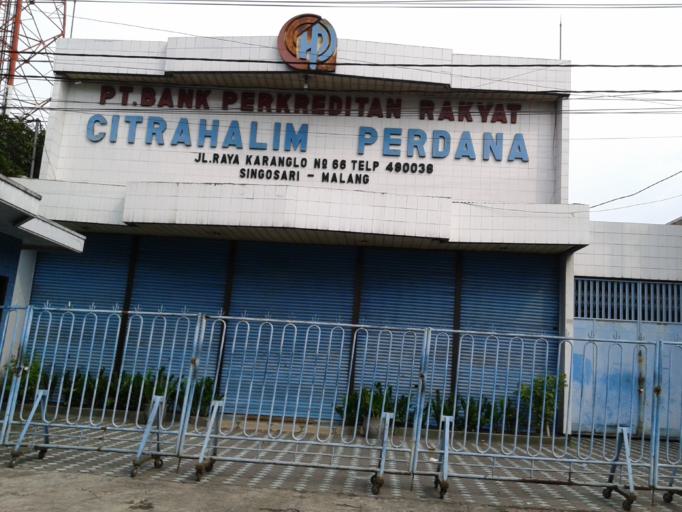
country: ID
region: East Java
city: Singosari
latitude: -7.9104
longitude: 112.6589
